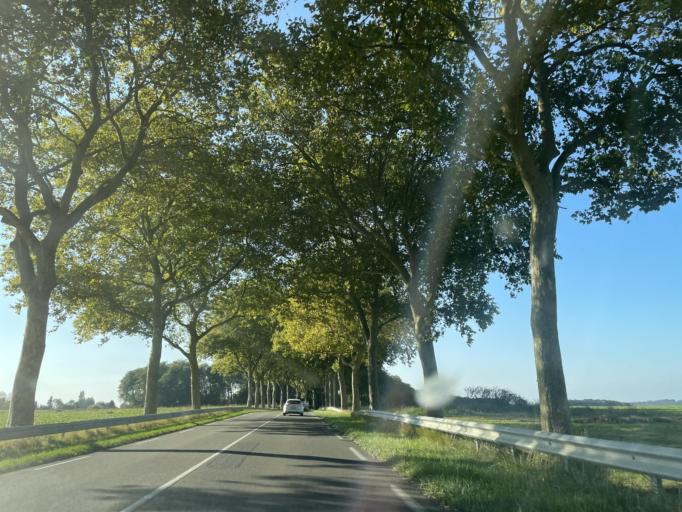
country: FR
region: Ile-de-France
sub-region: Departement de Seine-et-Marne
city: Guerard
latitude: 48.8408
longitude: 2.9602
